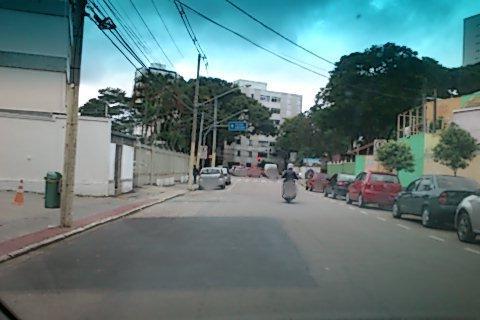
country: BR
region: Sao Paulo
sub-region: Sao Jose Dos Campos
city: Sao Jose dos Campos
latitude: -23.1962
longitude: -45.8907
